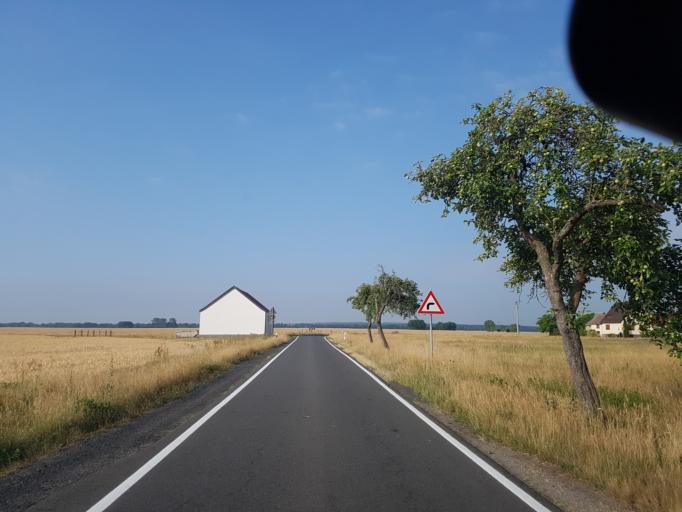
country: DE
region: Saxony-Anhalt
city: Jessen
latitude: 51.8509
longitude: 13.0376
